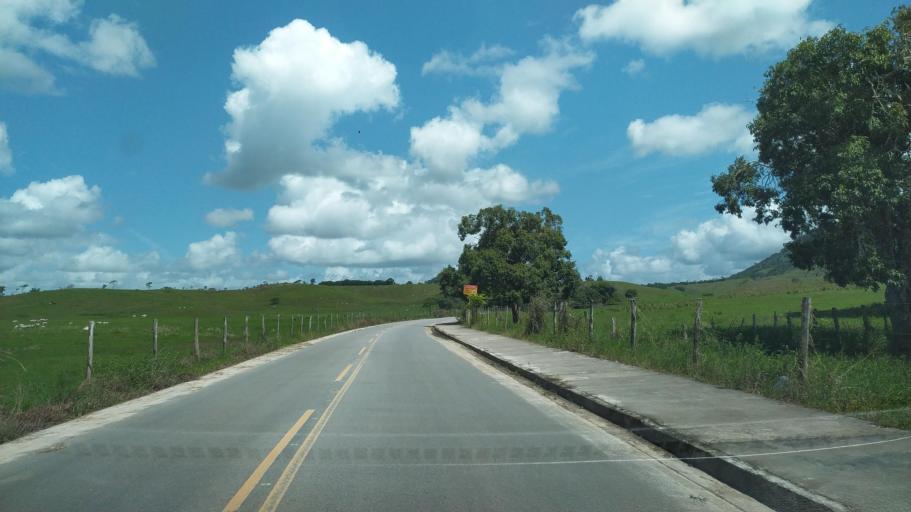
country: BR
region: Alagoas
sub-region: Uniao Dos Palmares
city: Uniao dos Palmares
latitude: -9.1605
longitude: -36.0463
